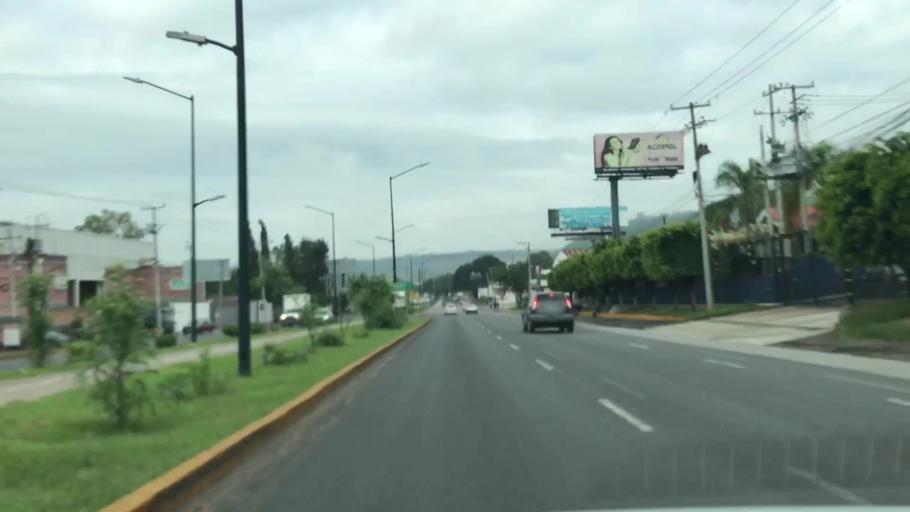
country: MX
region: Guanajuato
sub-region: Leon
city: Malagana (San Antonio del Monte)
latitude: 21.0897
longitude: -101.7382
